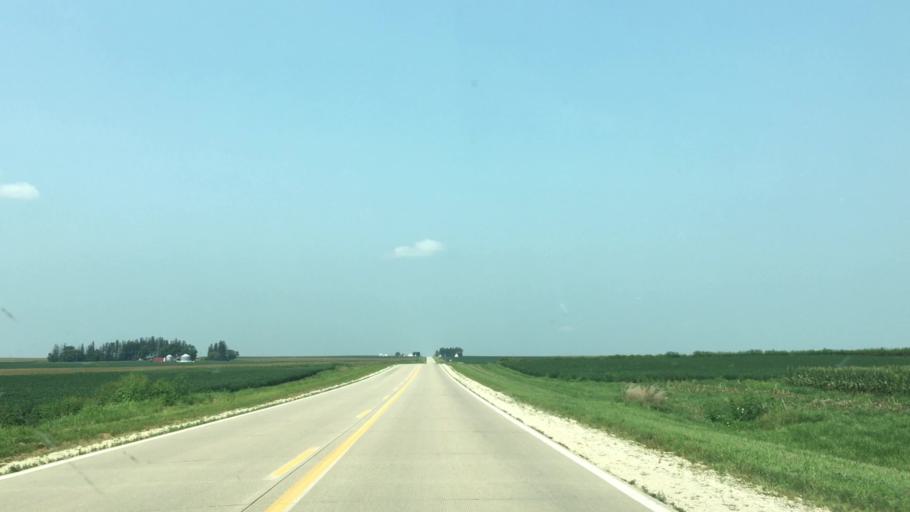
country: US
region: Iowa
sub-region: Fayette County
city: Oelwein
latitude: 42.6931
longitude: -91.8051
